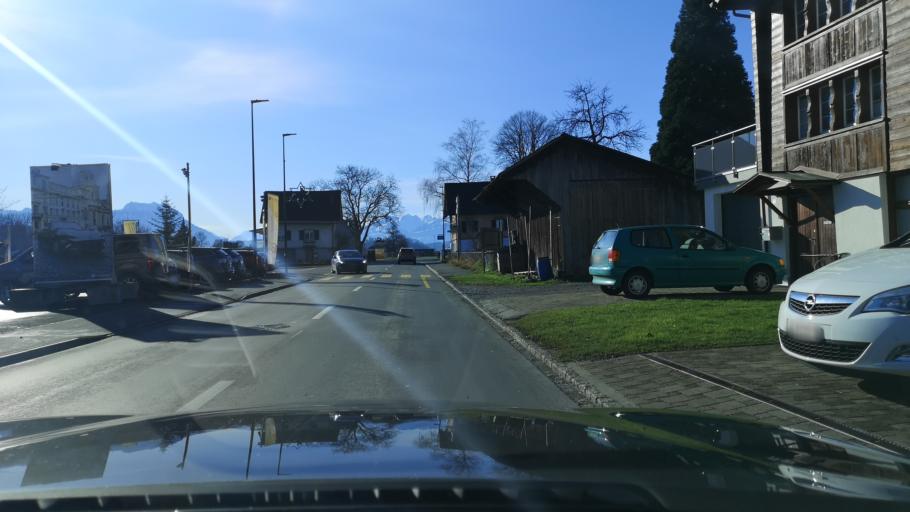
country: AT
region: Vorarlberg
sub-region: Politischer Bezirk Feldkirch
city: Mader
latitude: 47.3620
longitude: 9.6057
